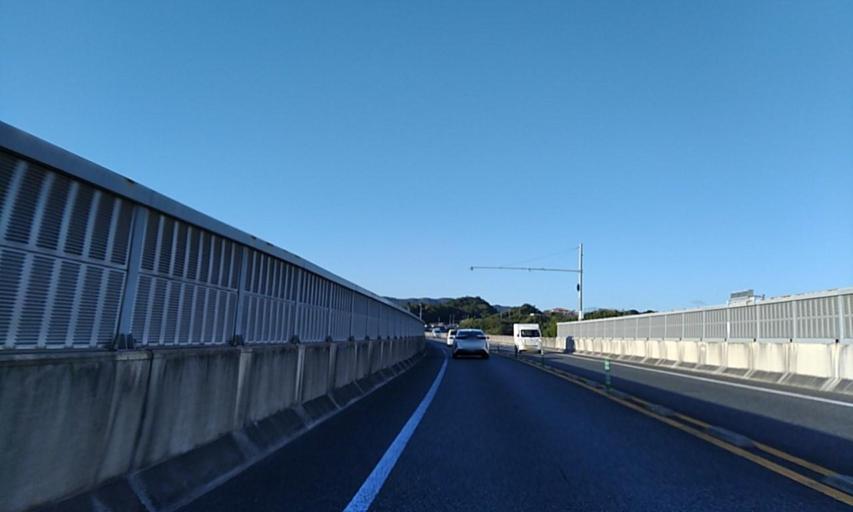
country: JP
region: Wakayama
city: Iwade
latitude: 34.3436
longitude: 135.2507
